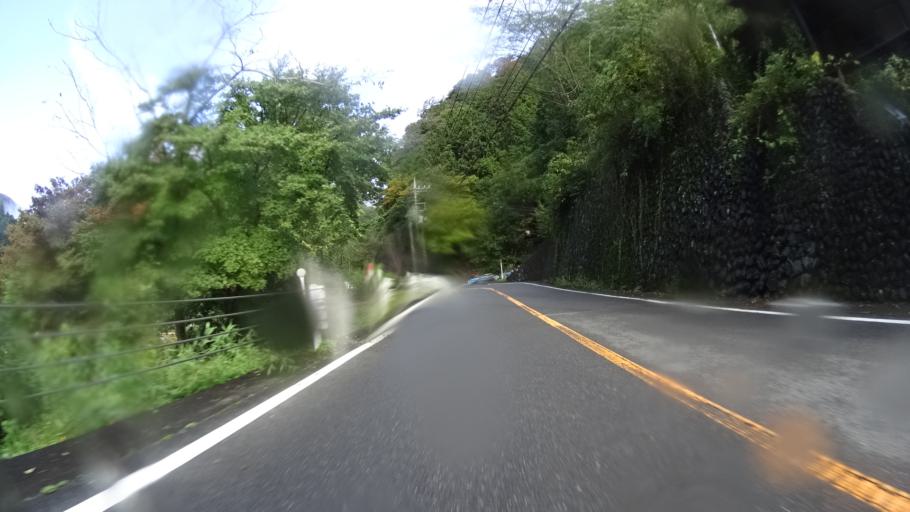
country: JP
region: Yamanashi
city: Otsuki
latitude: 35.7791
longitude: 138.9890
